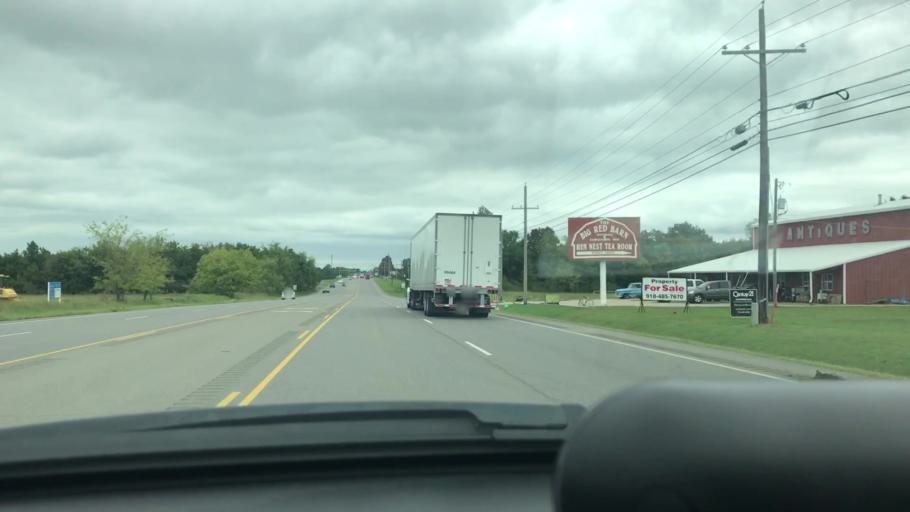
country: US
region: Oklahoma
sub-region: Wagoner County
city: Wagoner
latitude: 35.9382
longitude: -95.3952
